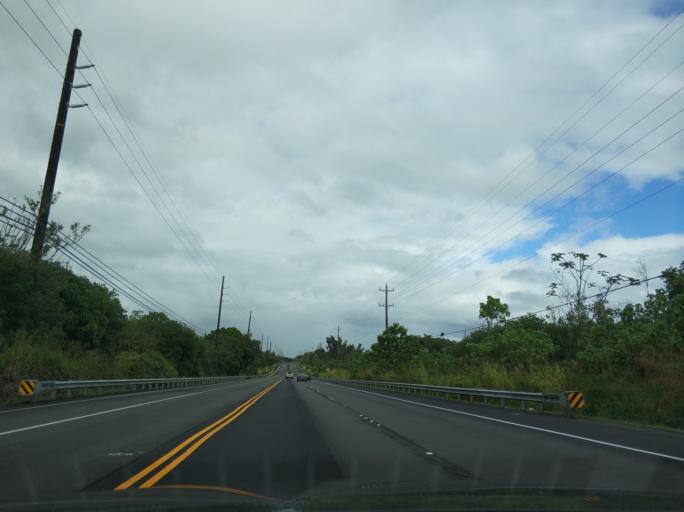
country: US
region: Hawaii
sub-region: Hawaii County
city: Kea'au
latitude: 19.5947
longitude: -155.0180
